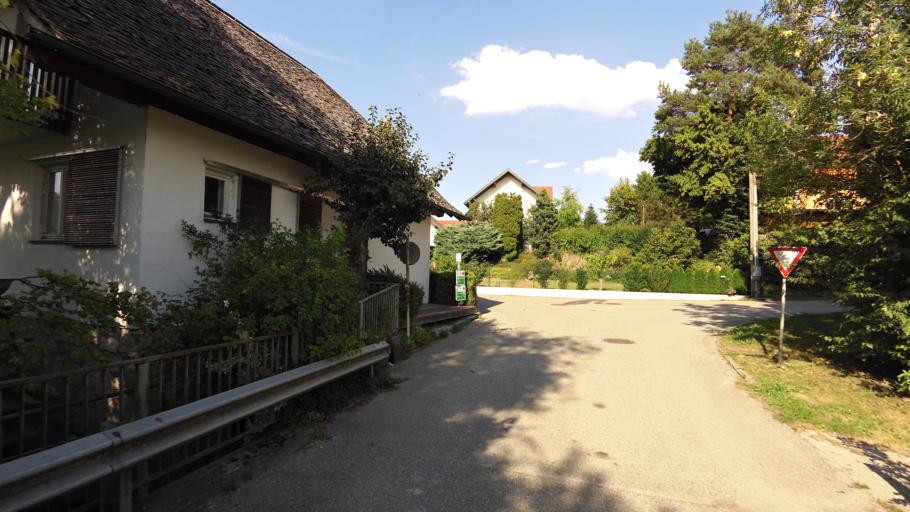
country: DE
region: Bavaria
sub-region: Lower Bavaria
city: Stubenberg
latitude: 48.2738
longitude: 13.1004
